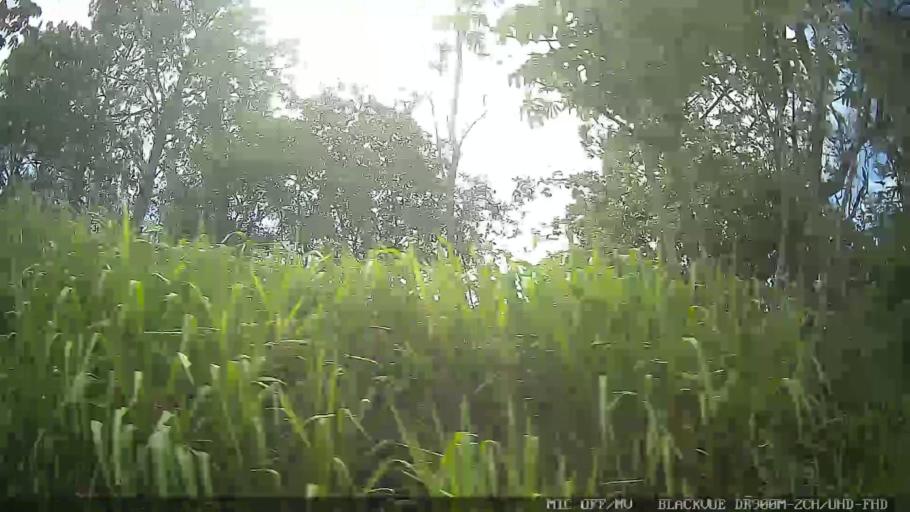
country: BR
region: Sao Paulo
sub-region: Conchas
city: Conchas
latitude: -22.9513
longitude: -47.9834
